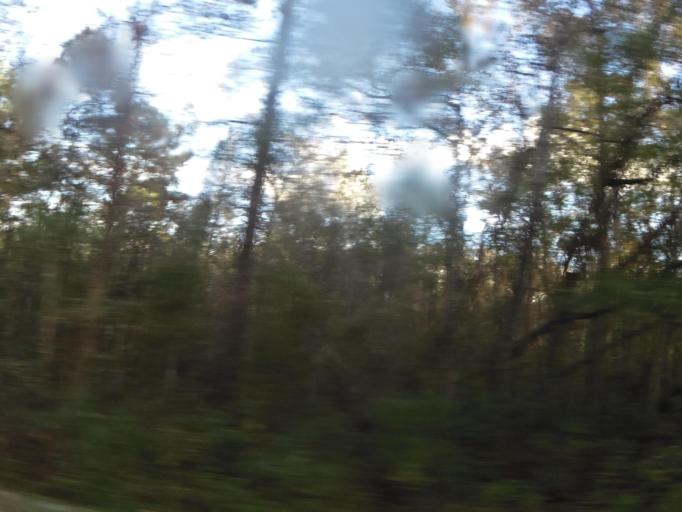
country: US
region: Florida
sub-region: Duval County
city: Baldwin
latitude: 30.1800
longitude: -81.9915
